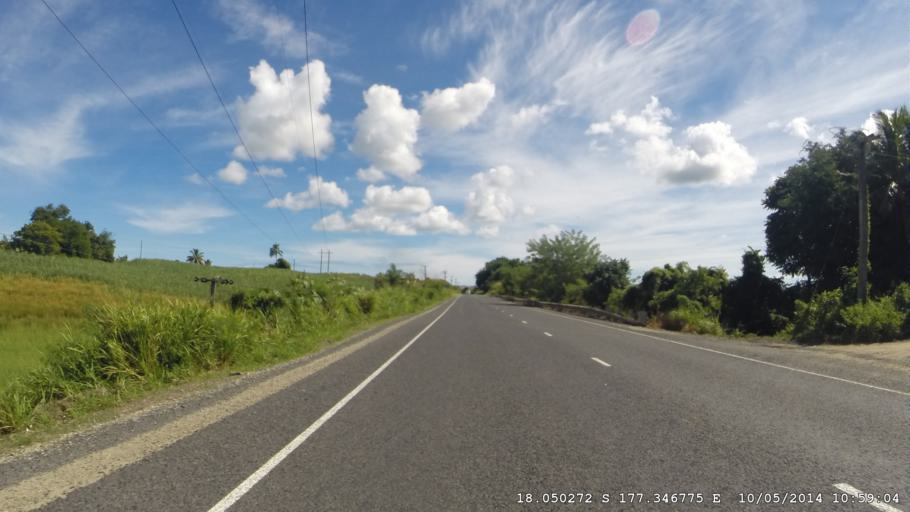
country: FJ
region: Western
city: Nadi
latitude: -18.0503
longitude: 177.3468
